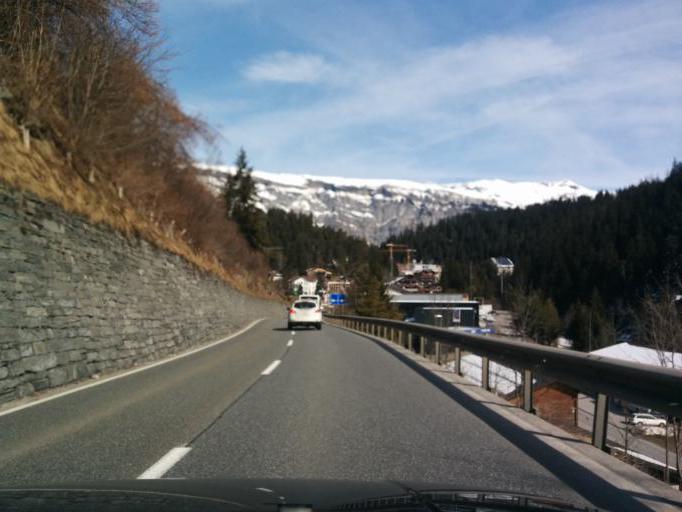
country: CH
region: Grisons
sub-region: Surselva District
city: Laax
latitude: 46.8096
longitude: 9.2612
